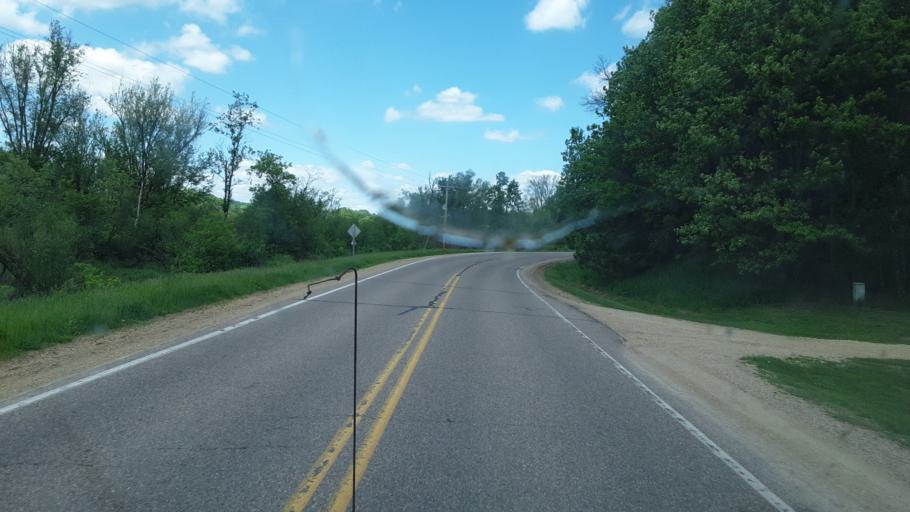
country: US
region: Wisconsin
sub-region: Sauk County
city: Reedsburg
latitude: 43.5667
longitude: -89.9989
